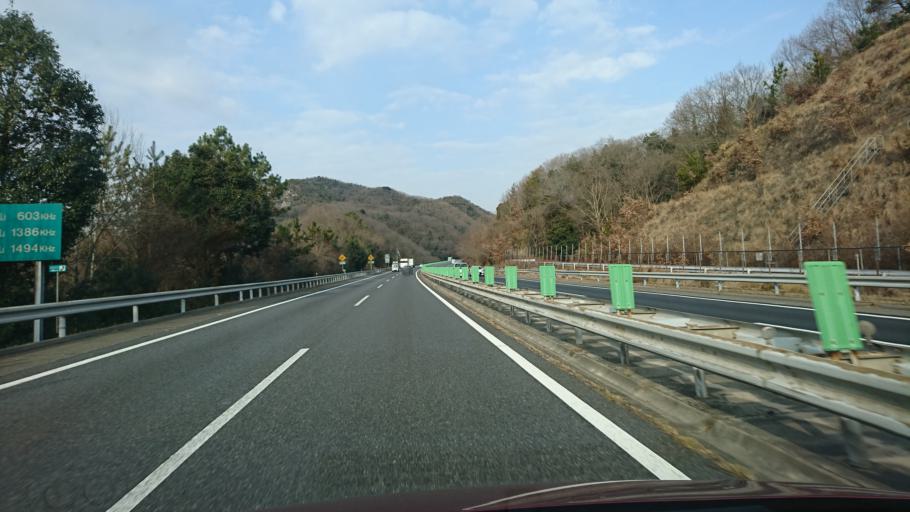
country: JP
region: Hyogo
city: Kariya
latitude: 34.7825
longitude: 134.2217
